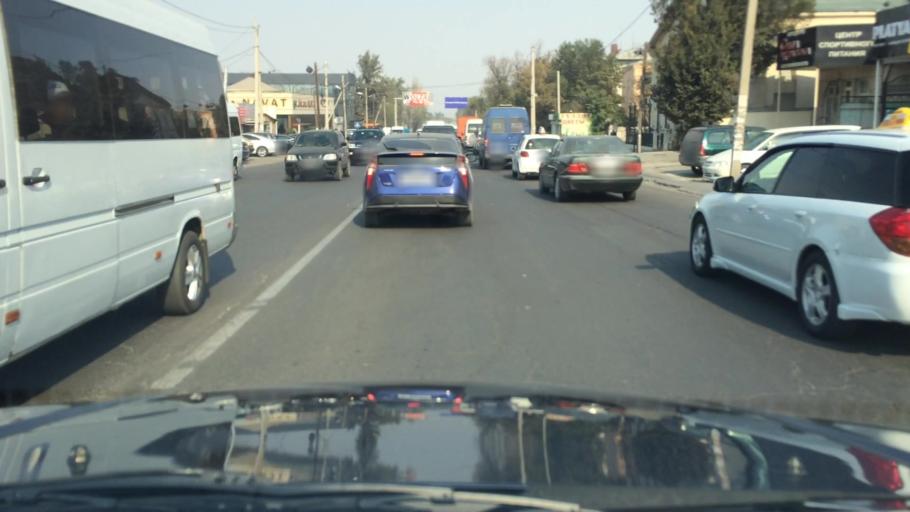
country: KG
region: Chuy
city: Lebedinovka
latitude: 42.8809
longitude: 74.6371
